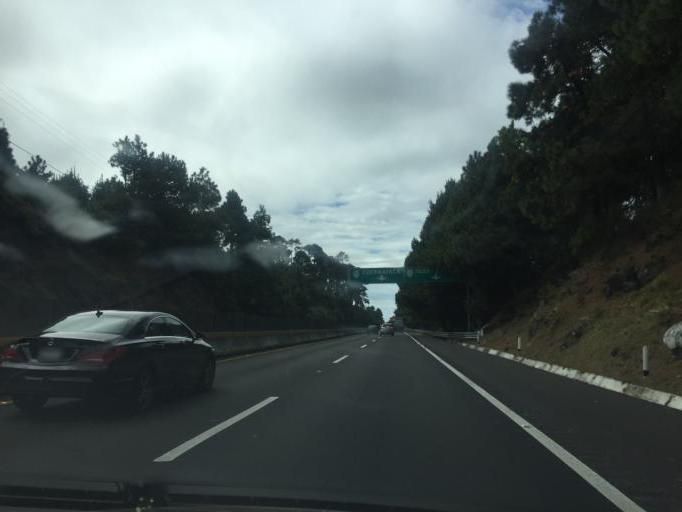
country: MX
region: Morelos
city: Tres Marias
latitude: 19.0780
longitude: -99.2333
